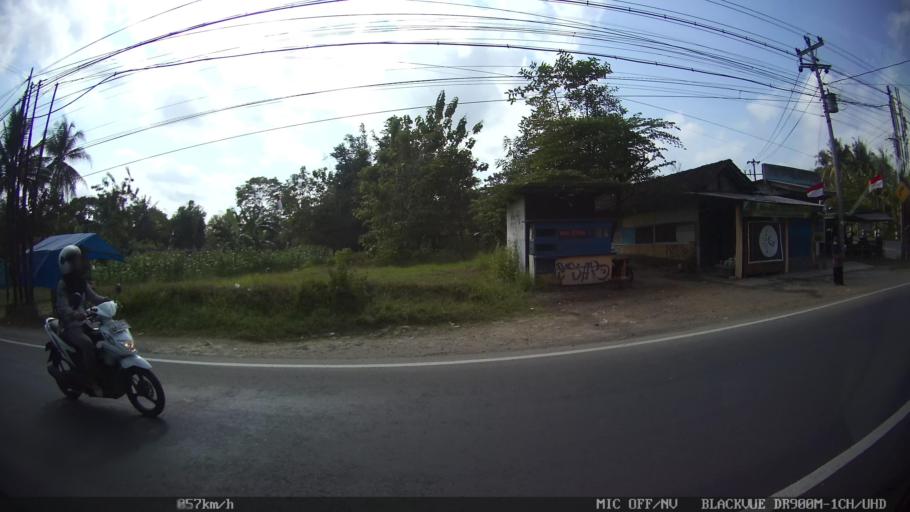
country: ID
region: Daerah Istimewa Yogyakarta
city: Srandakan
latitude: -7.8494
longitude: 110.2176
